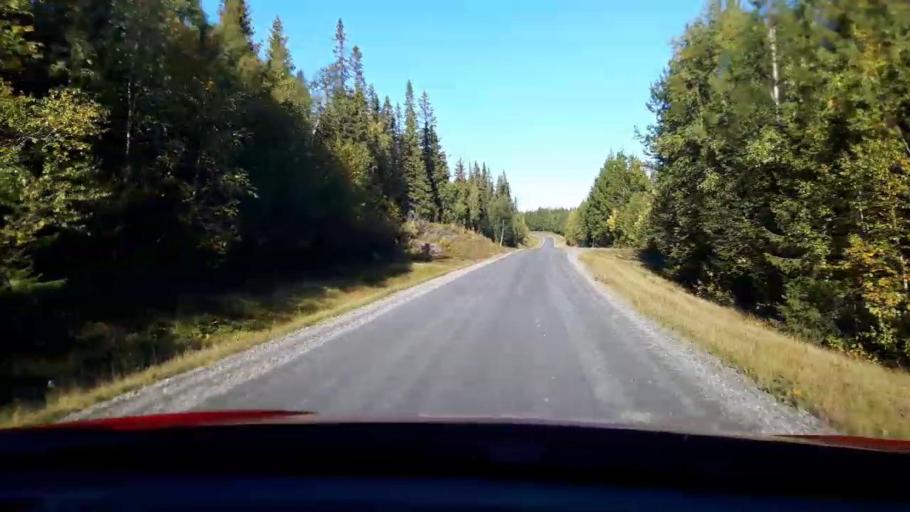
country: NO
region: Nord-Trondelag
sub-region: Lierne
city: Sandvika
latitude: 64.5307
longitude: 14.0408
